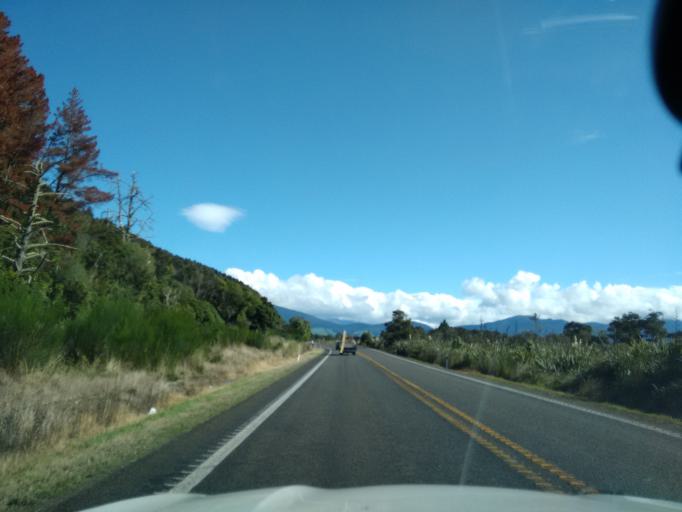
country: NZ
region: Waikato
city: Turangi
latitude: -38.9389
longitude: 175.8596
